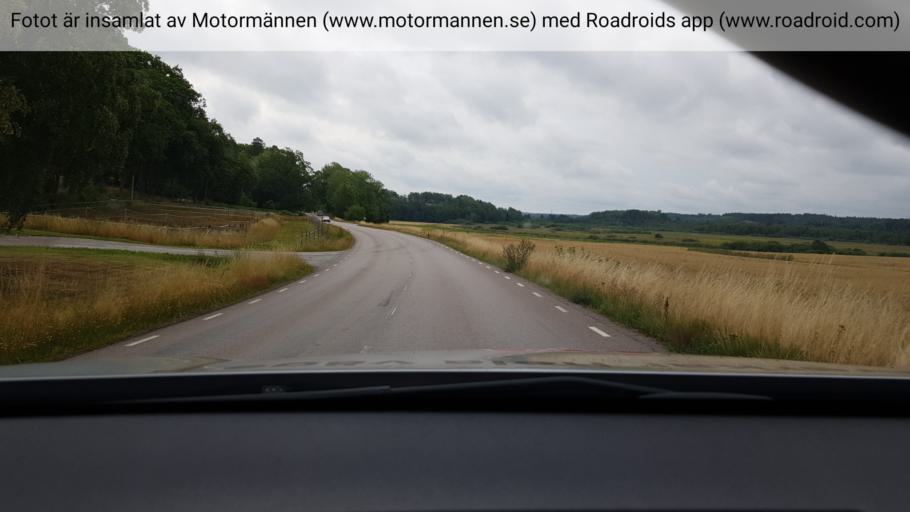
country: SE
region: Soedermanland
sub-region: Gnesta Kommun
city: Gnesta
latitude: 59.0807
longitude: 17.2691
